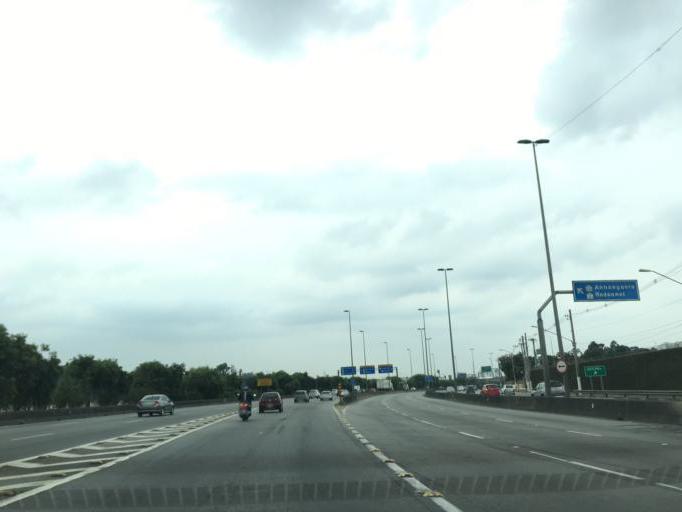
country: BR
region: Sao Paulo
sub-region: Osasco
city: Osasco
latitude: -23.5189
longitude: -46.7444
